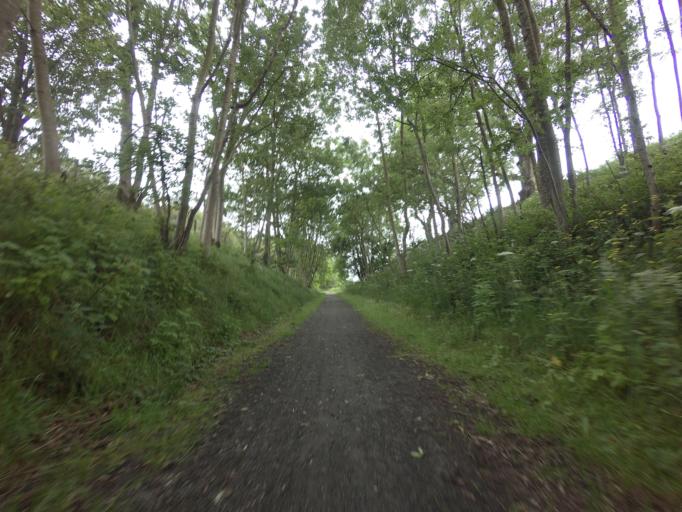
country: GB
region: Scotland
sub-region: Aberdeenshire
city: Mintlaw
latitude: 57.5122
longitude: -2.1403
